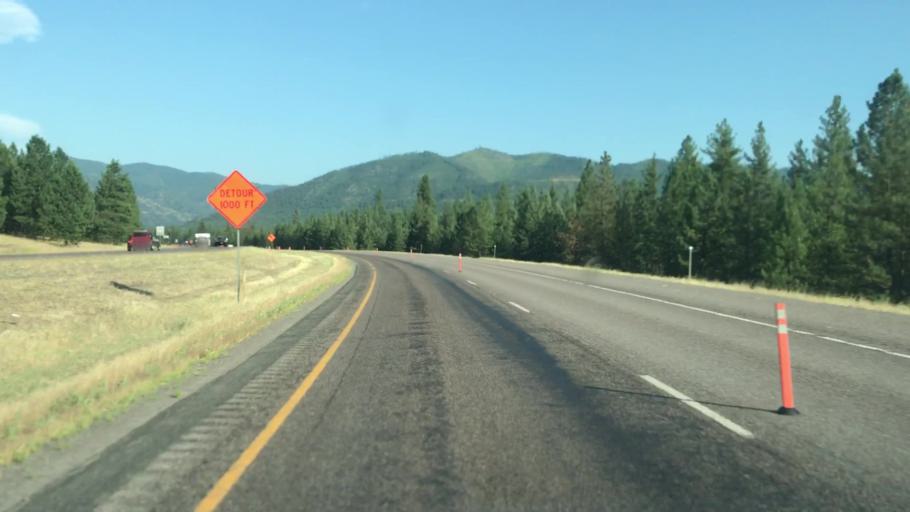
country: US
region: Montana
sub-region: Mineral County
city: Superior
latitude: 47.0156
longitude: -114.7337
